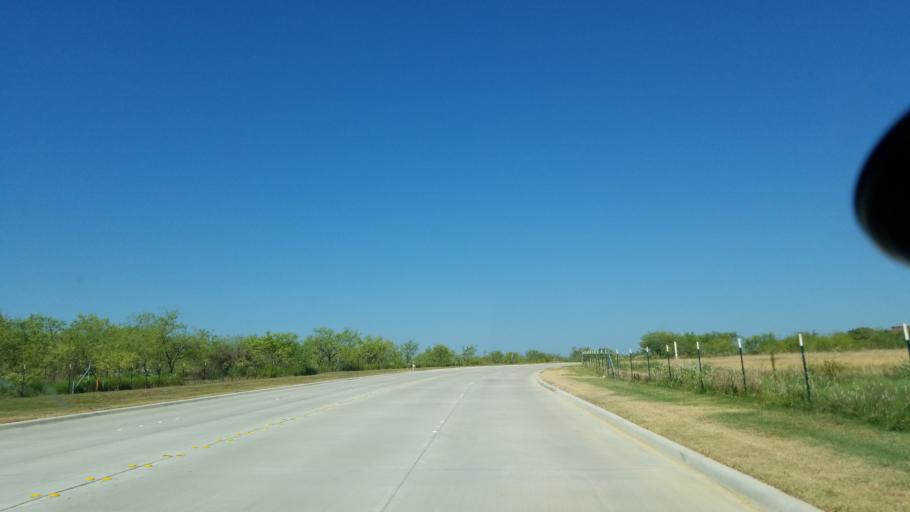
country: US
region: Texas
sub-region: Tarrant County
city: Mansfield
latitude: 32.5607
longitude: -97.1017
